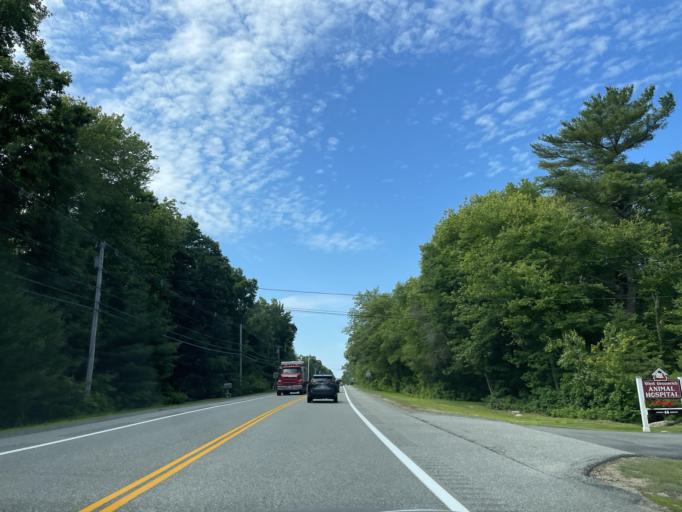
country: US
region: Rhode Island
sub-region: Kent County
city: West Greenwich
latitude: 41.6569
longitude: -71.6949
